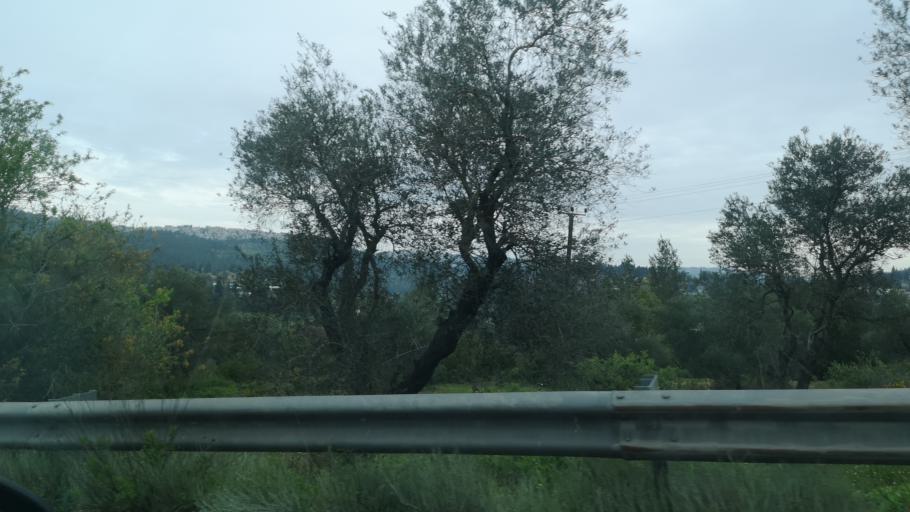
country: PS
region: West Bank
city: Bayt Iksa
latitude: 31.7714
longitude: 35.1572
